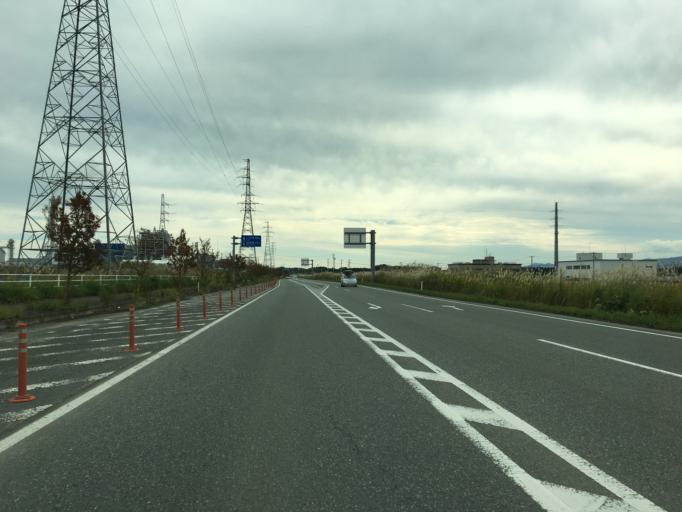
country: JP
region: Miyagi
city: Marumori
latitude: 37.8365
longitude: 140.9380
